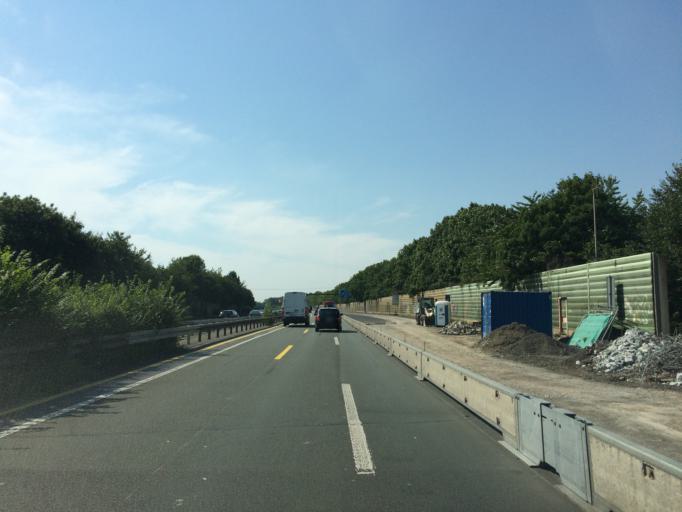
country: DE
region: North Rhine-Westphalia
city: Lunen
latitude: 51.5789
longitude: 7.5056
